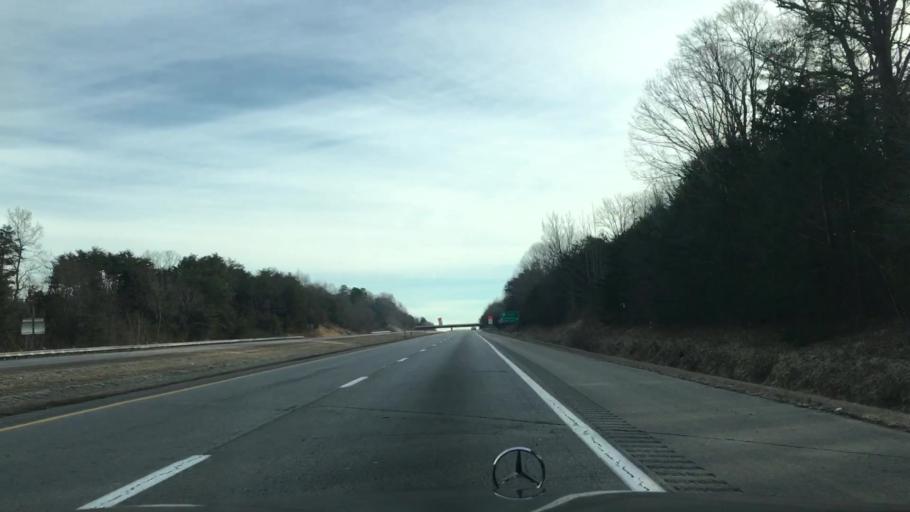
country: US
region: Virginia
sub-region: City of Danville
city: Danville
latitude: 36.5458
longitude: -79.4091
